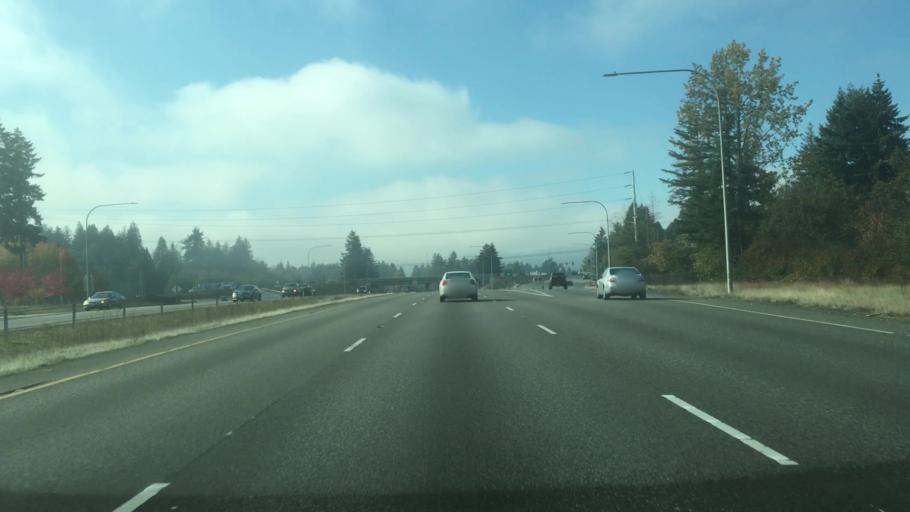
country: US
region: Washington
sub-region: Thurston County
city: Tumwater
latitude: 47.0259
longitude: -122.9181
